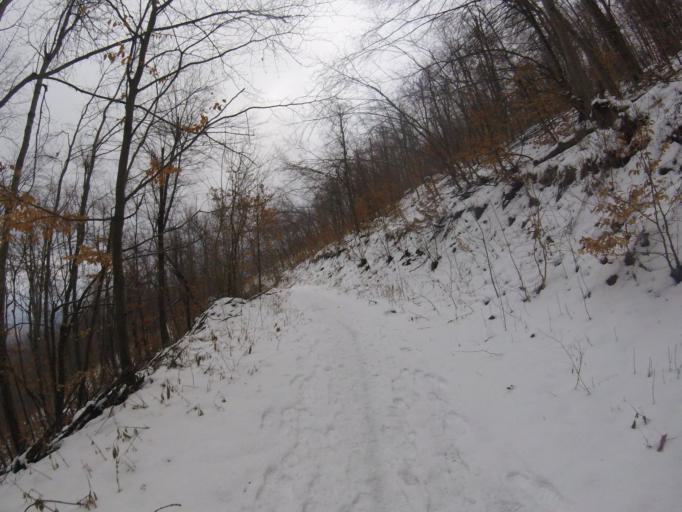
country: HU
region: Pest
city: Dunabogdany
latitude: 47.7516
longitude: 19.0136
